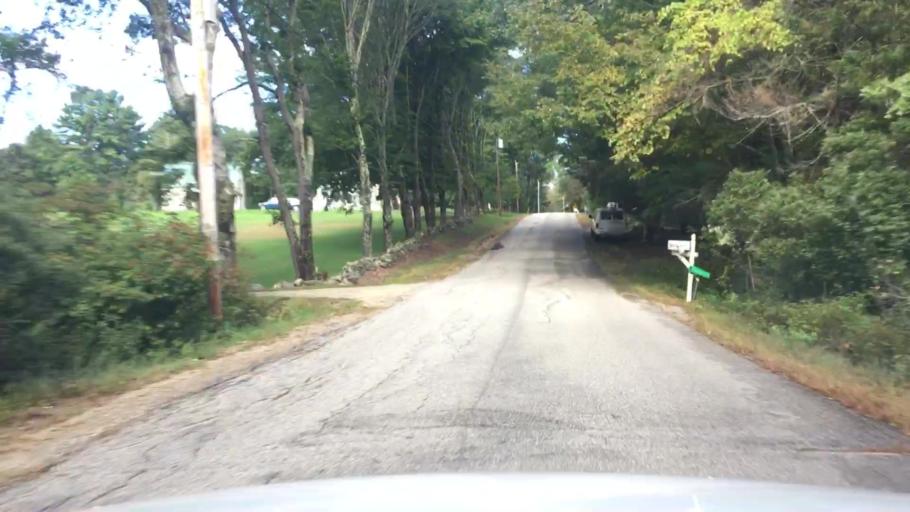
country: US
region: Maine
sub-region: York County
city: York Harbor
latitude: 43.1181
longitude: -70.6771
